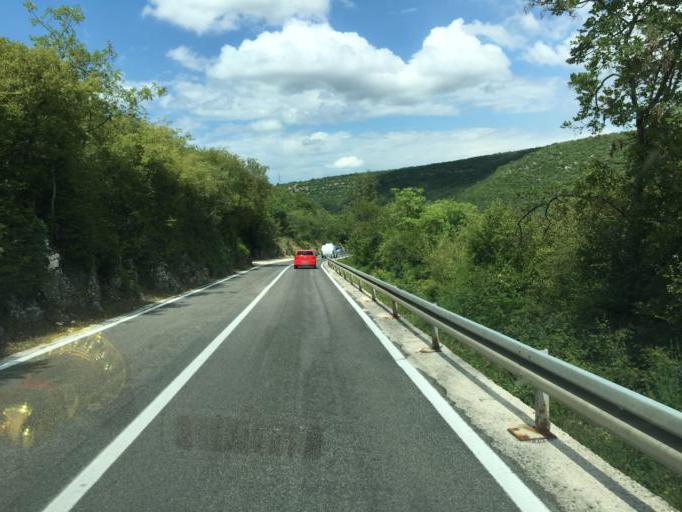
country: HR
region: Istarska
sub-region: Grad Rovinj
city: Rovinj
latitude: 45.1214
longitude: 13.7544
